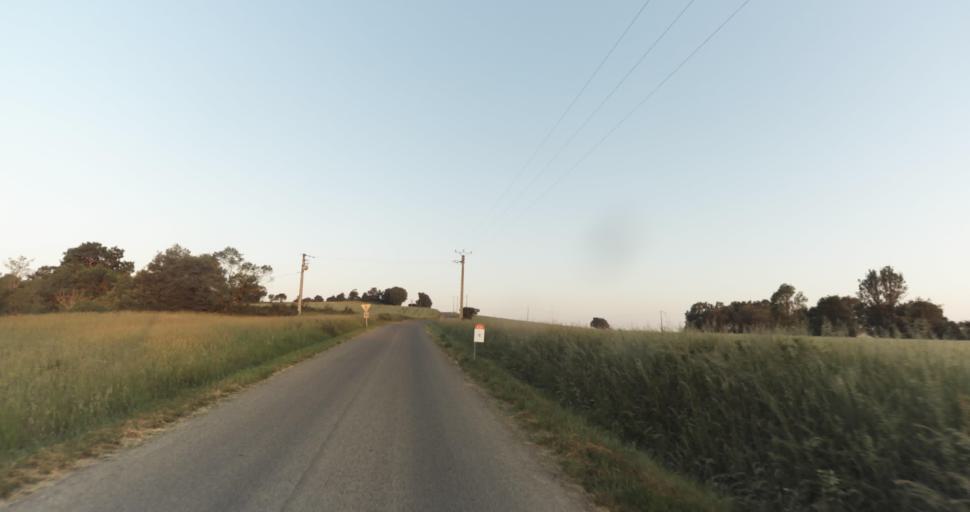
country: FR
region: Midi-Pyrenees
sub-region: Departement du Gers
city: Pujaudran
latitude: 43.6480
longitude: 1.1360
